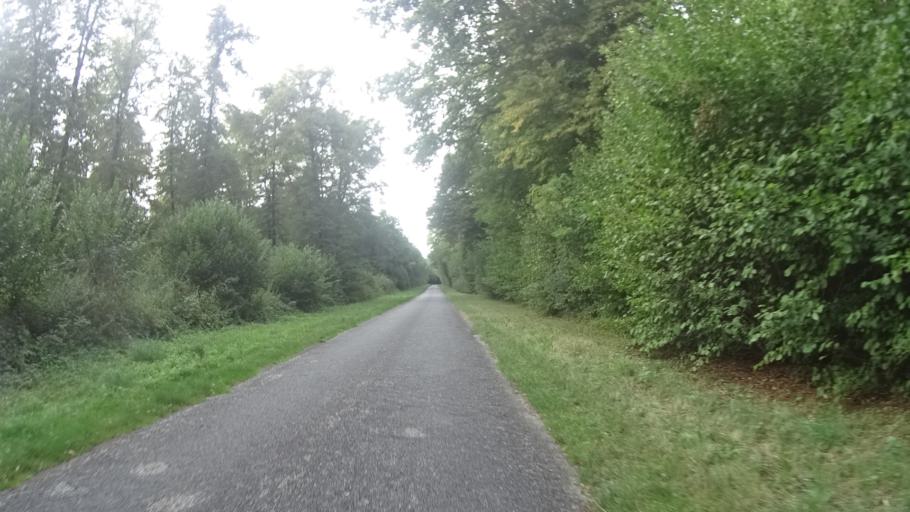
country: FR
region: Picardie
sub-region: Departement de l'Oise
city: Ver-sur-Launette
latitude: 49.1602
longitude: 2.6808
